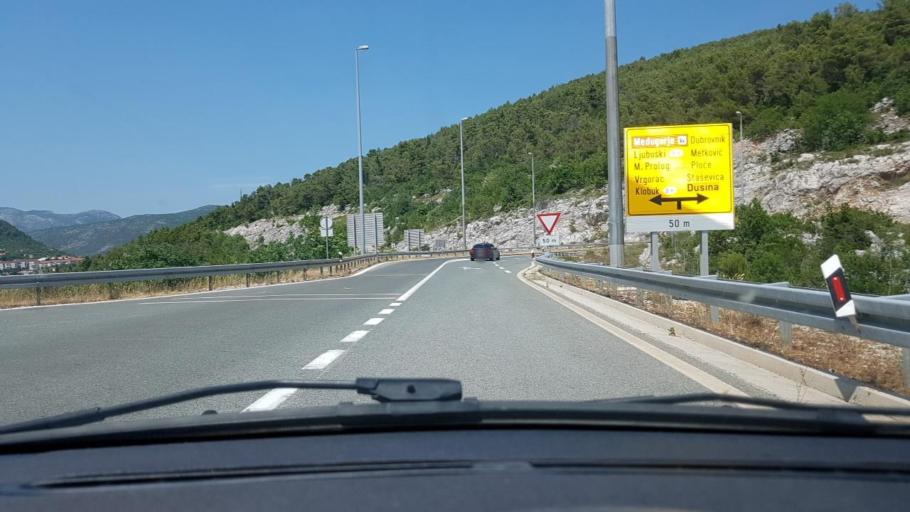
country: HR
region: Splitsko-Dalmatinska
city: Vrgorac
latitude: 43.1925
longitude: 17.3791
